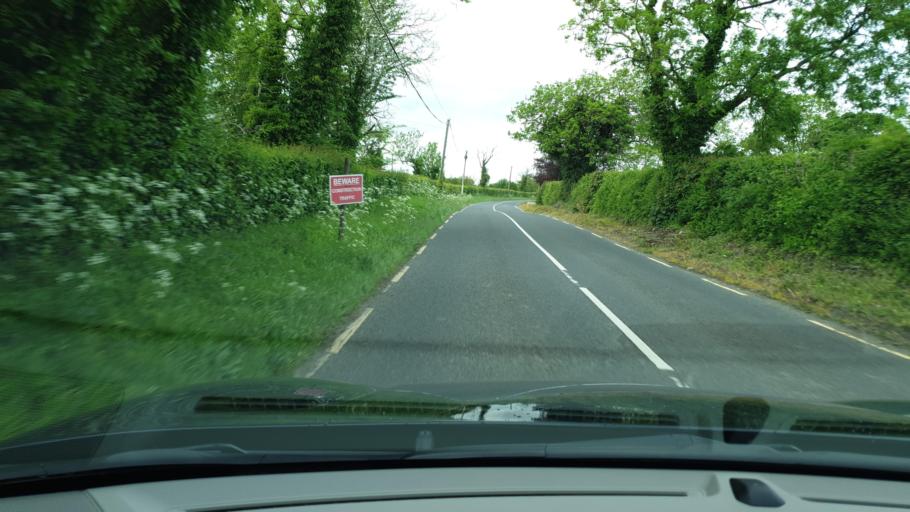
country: IE
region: Leinster
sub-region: An Mhi
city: Ratoath
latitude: 53.4791
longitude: -6.4287
